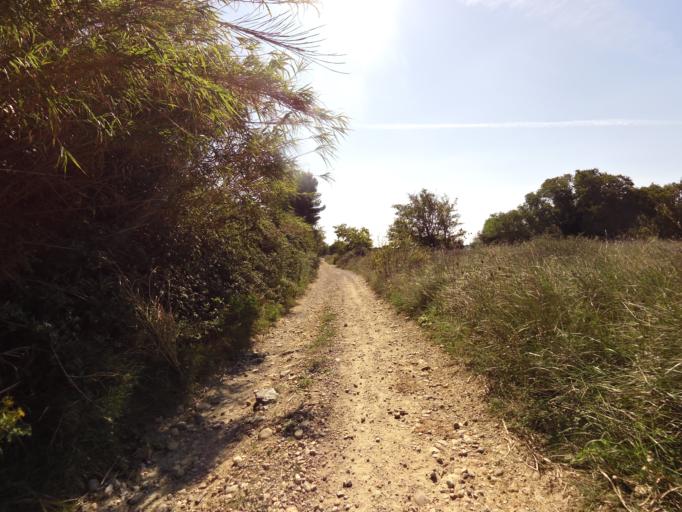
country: FR
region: Languedoc-Roussillon
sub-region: Departement du Gard
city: Gallargues-le-Montueux
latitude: 43.7297
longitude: 4.1684
